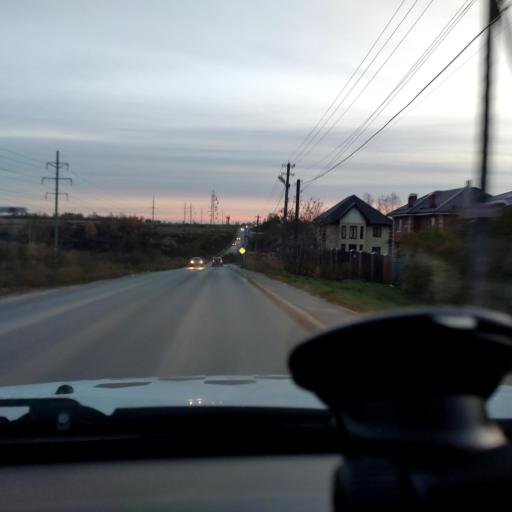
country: RU
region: Perm
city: Perm
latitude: 58.0124
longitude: 56.3224
